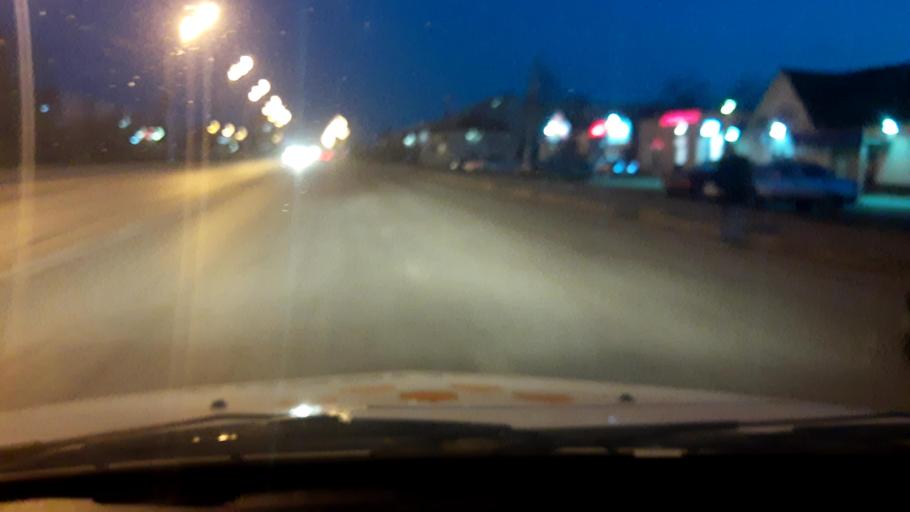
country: RU
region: Bashkortostan
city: Iglino
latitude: 54.7623
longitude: 56.2411
